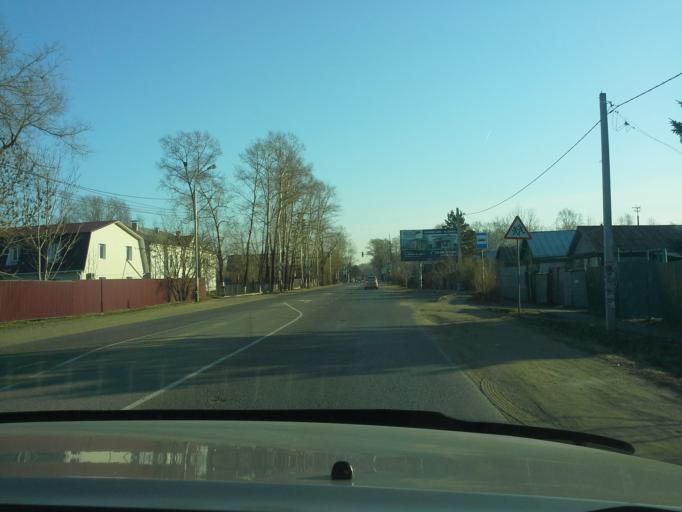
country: RU
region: Khabarovsk Krai
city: Topolevo
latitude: 48.4697
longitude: 135.1784
